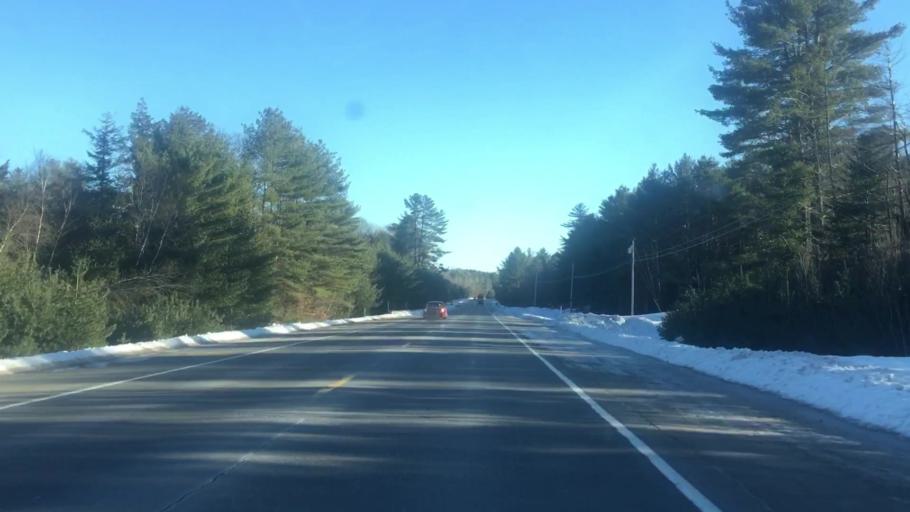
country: US
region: Maine
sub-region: Somerset County
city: Norridgewock
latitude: 44.6895
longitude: -69.7391
